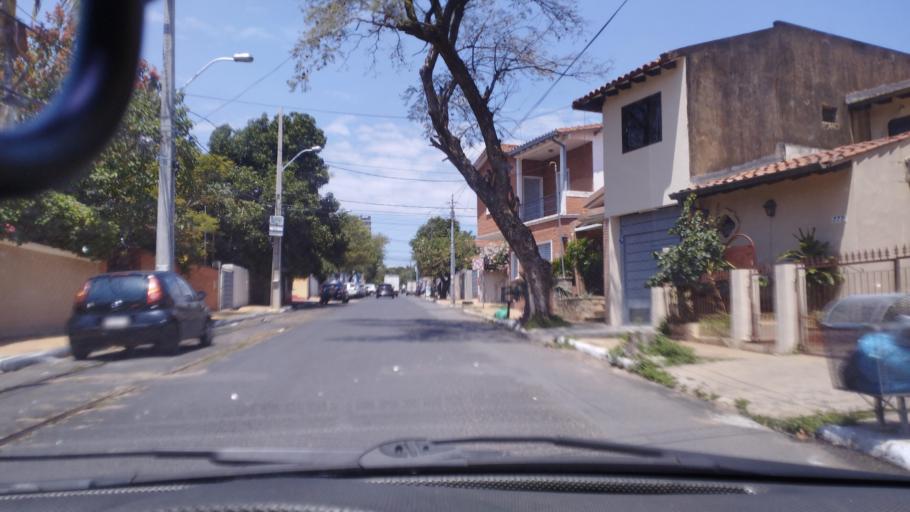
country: PY
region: Asuncion
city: Asuncion
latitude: -25.2821
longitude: -57.6123
